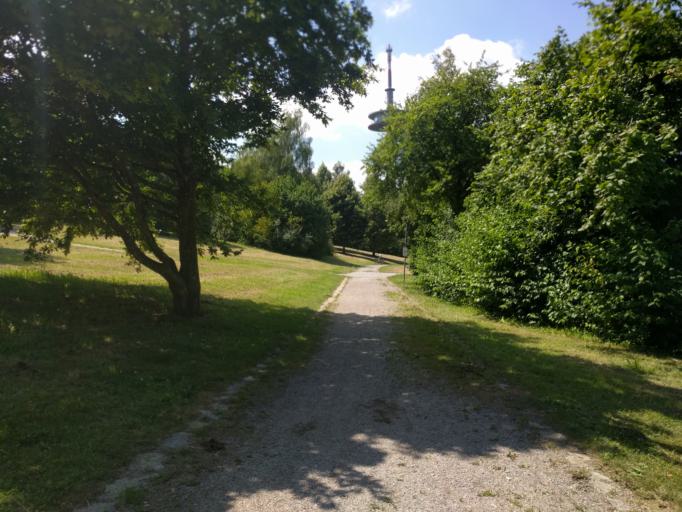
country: DE
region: Bavaria
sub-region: Upper Palatinate
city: Pentling
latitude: 48.9936
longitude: 12.0808
